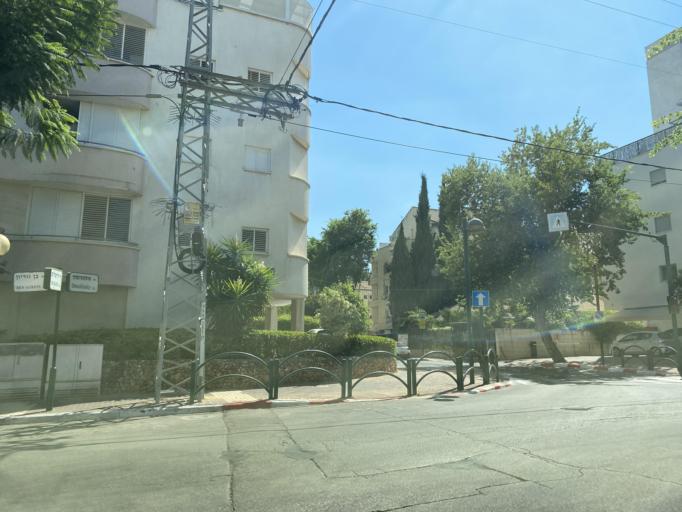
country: IL
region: Central District
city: Kfar Saba
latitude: 32.1732
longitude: 34.9050
